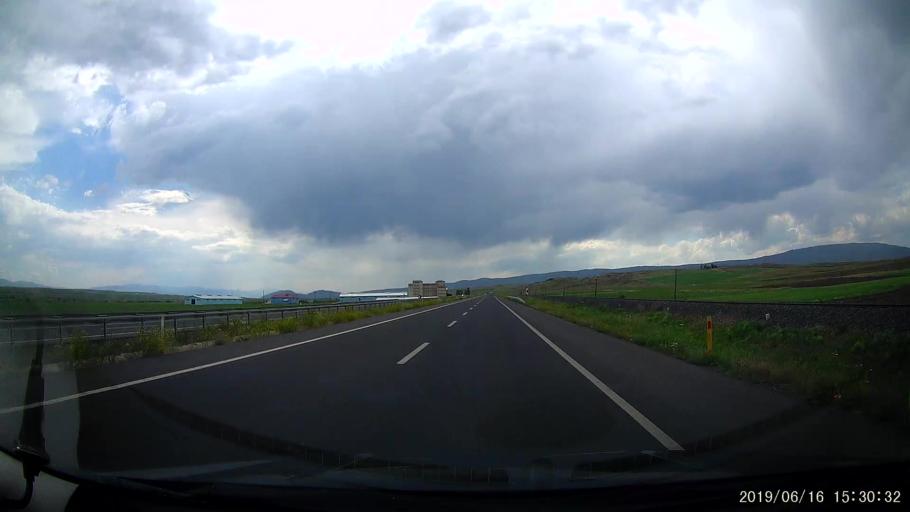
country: TR
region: Erzurum
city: Horasan
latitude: 40.0339
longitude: 42.1024
